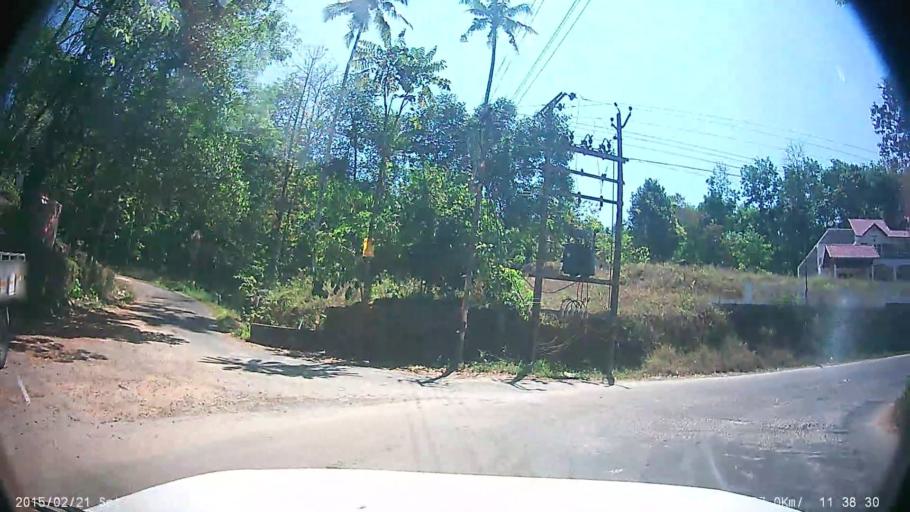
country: IN
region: Kerala
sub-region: Kottayam
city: Lalam
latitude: 9.8061
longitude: 76.7309
